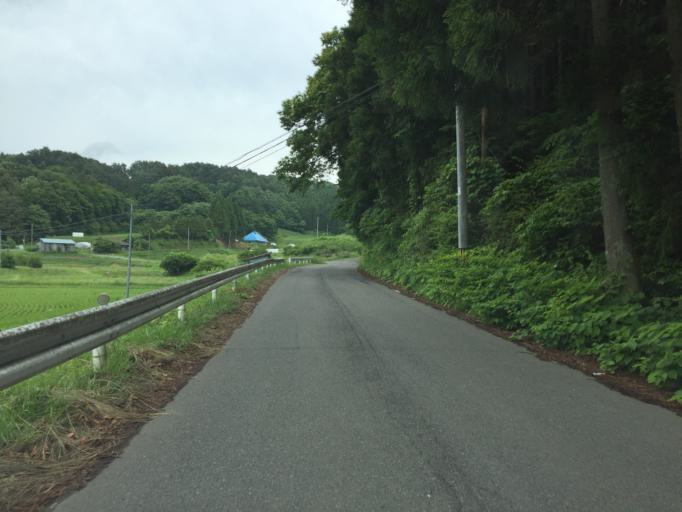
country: JP
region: Fukushima
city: Funehikimachi-funehiki
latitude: 37.3966
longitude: 140.6719
